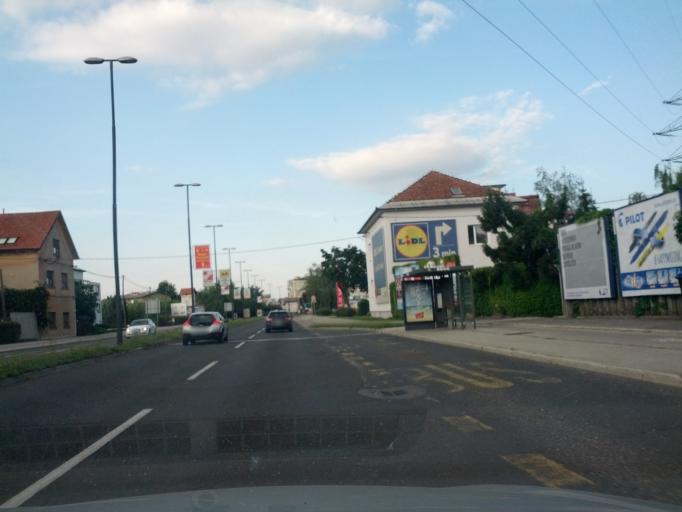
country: SI
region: Ljubljana
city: Ljubljana
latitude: 46.0671
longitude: 14.5344
